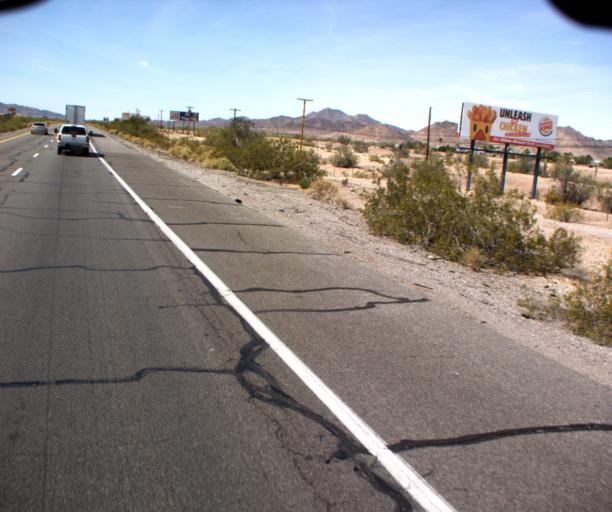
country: US
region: Arizona
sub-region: La Paz County
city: Quartzsite
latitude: 33.6591
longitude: -114.2466
